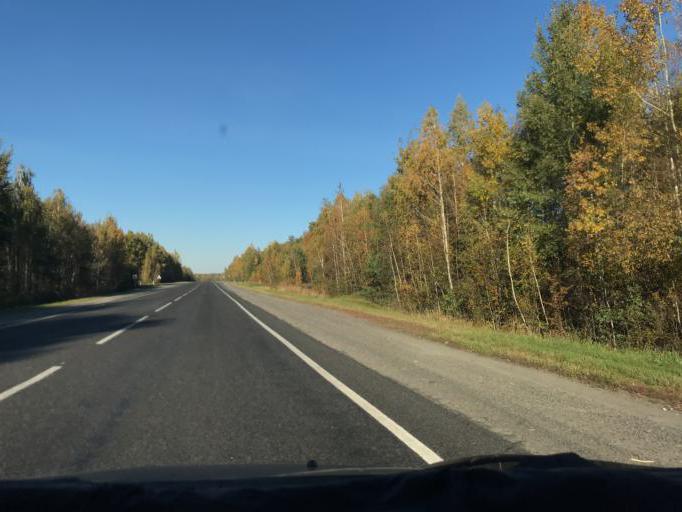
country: BY
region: Gomel
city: Kalinkavichy
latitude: 52.1028
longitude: 29.3692
